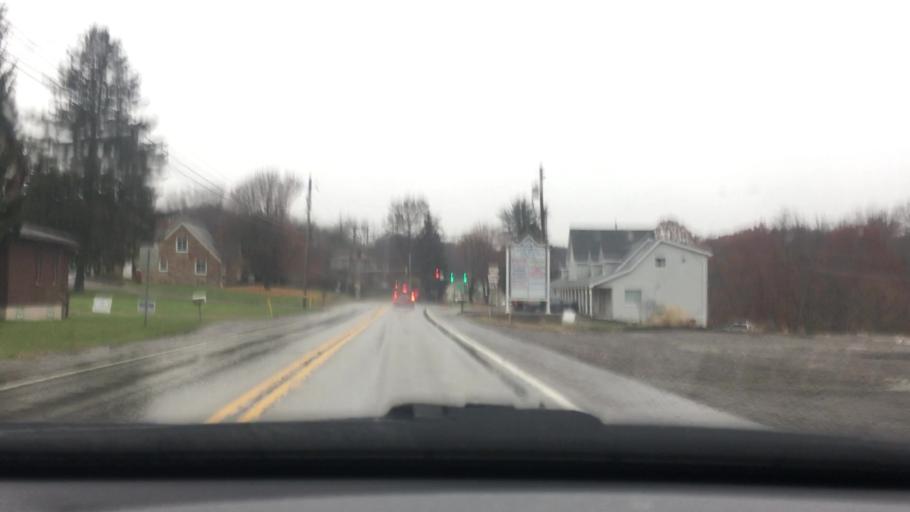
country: US
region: Pennsylvania
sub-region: Butler County
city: Saxonburg
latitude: 40.7180
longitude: -79.7547
